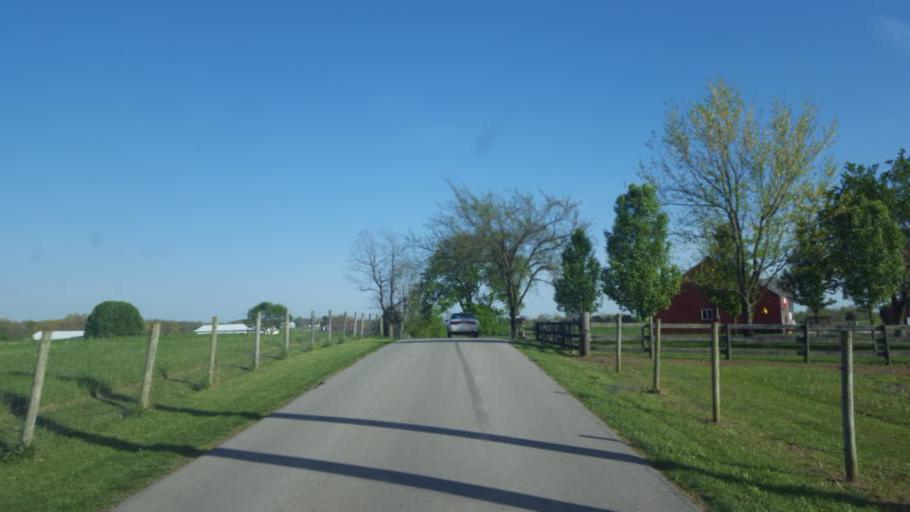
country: US
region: Kentucky
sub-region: Barren County
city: Cave City
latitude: 37.1707
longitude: -85.9887
